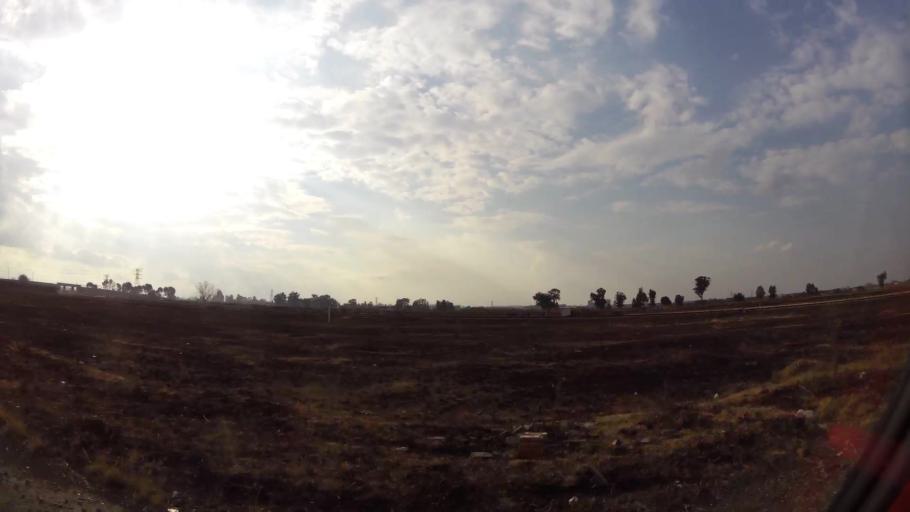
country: ZA
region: Gauteng
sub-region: Sedibeng District Municipality
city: Vereeniging
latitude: -26.6777
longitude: 27.9017
